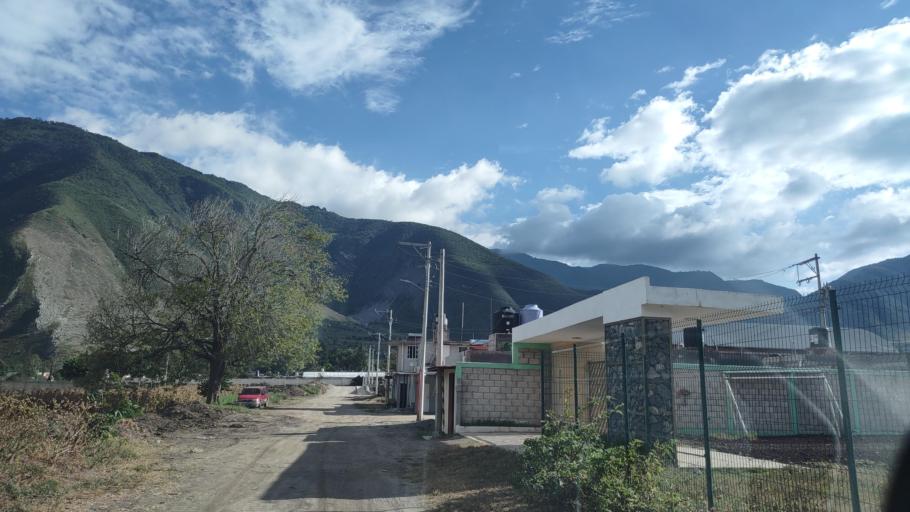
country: MX
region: Veracruz
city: Acultzingo
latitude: 18.7229
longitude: -97.3056
